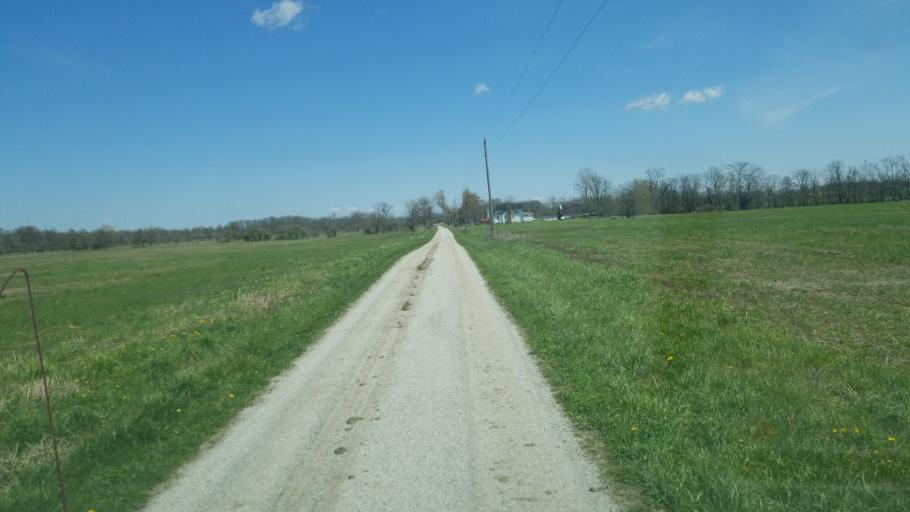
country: US
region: Ohio
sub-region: Marion County
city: Prospect
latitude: 40.4555
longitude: -83.2434
